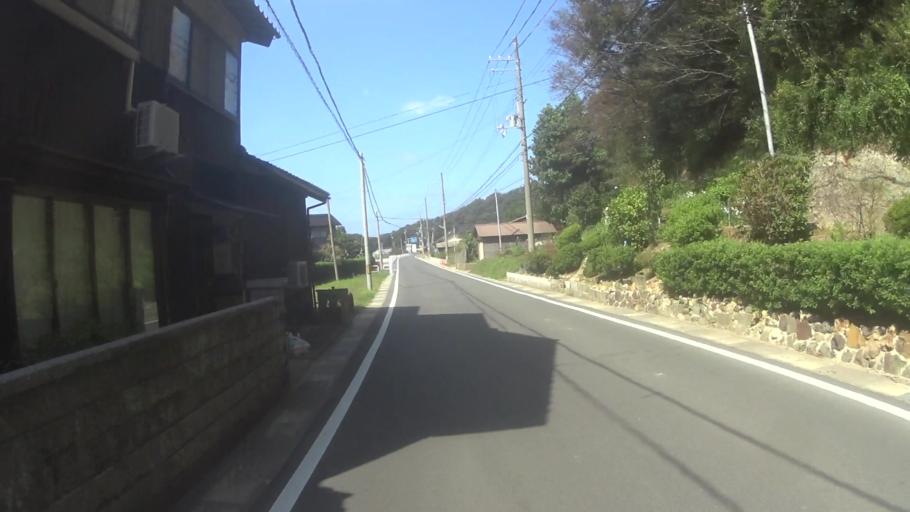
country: JP
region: Kyoto
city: Miyazu
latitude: 35.7377
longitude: 135.1110
